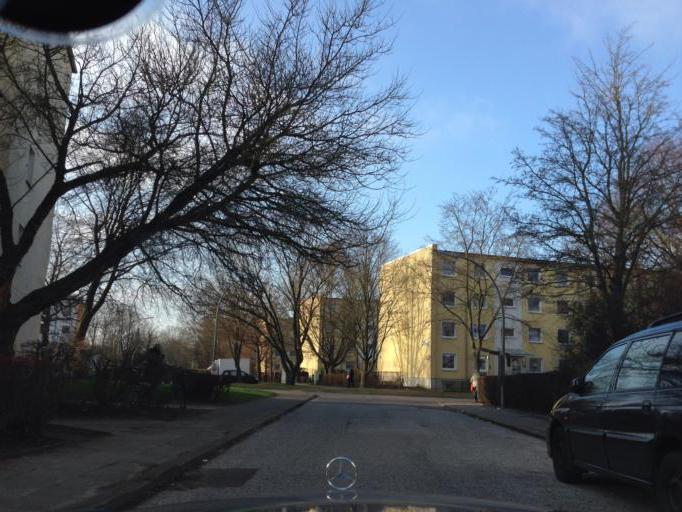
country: DE
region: Schleswig-Holstein
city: Stapelfeld
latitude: 53.5986
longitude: 10.1829
